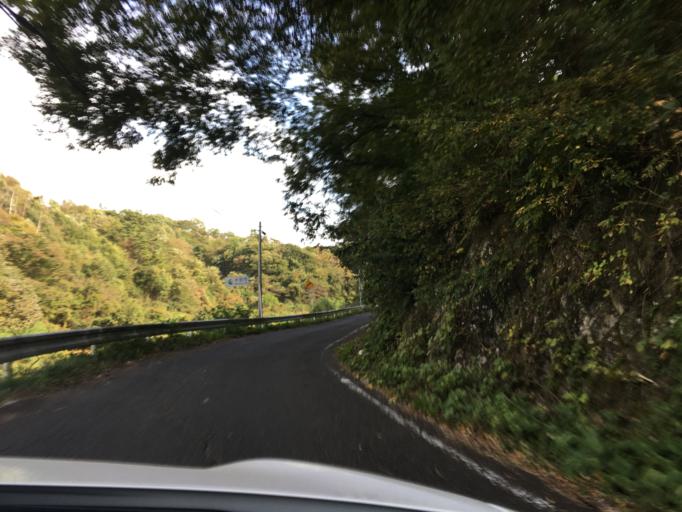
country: JP
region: Fukushima
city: Nihommatsu
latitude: 37.5257
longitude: 140.5032
